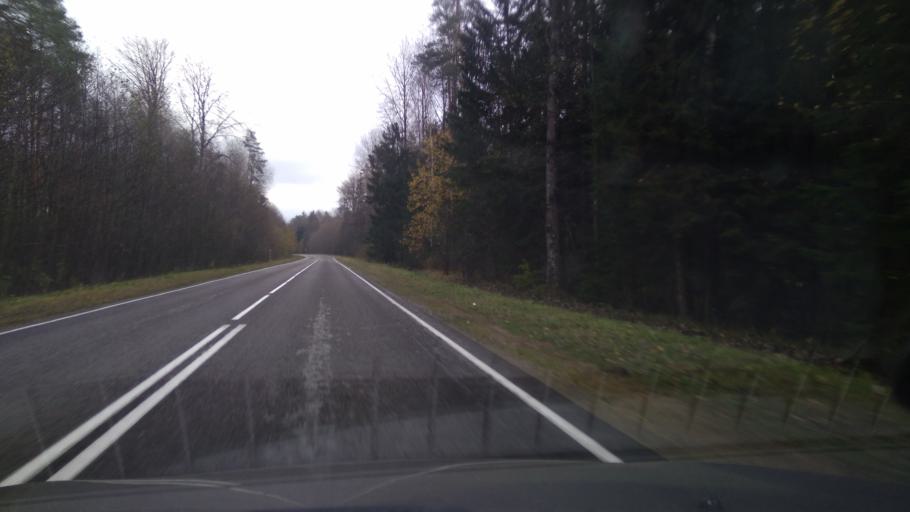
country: BY
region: Minsk
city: Urechcha
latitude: 53.2175
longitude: 27.8432
